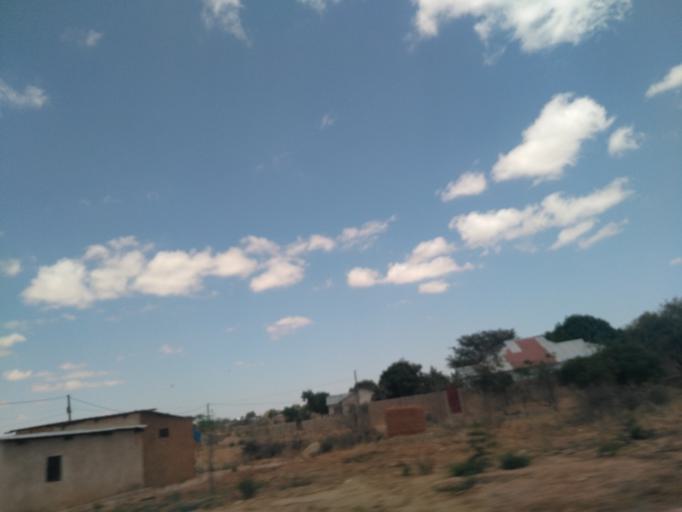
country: TZ
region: Dodoma
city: Kisasa
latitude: -6.1786
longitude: 35.7862
